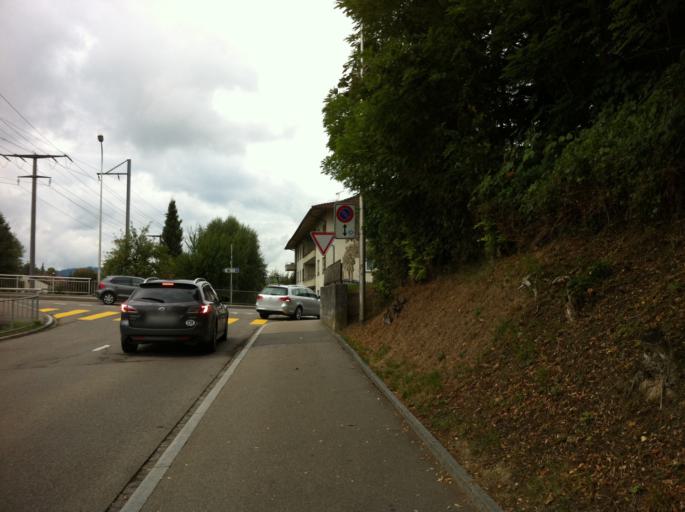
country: CH
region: Saint Gallen
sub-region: Wahlkreis St. Gallen
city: Gossau
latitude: 47.4117
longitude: 9.2499
